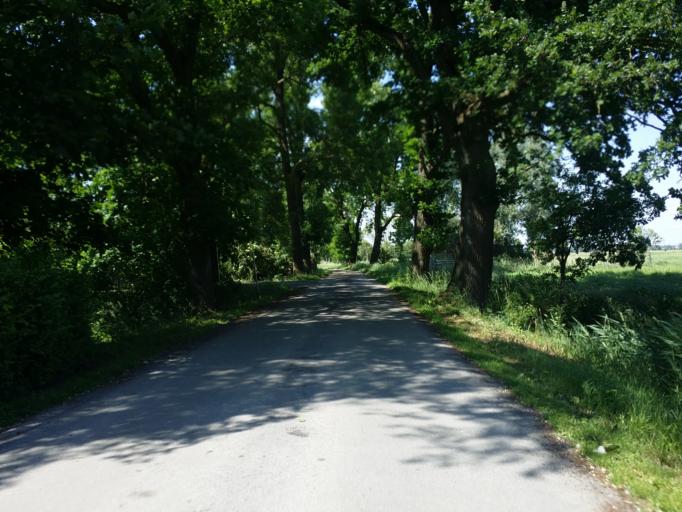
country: DE
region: Lower Saxony
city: Neuenkirchen
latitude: 53.1657
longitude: 8.5107
